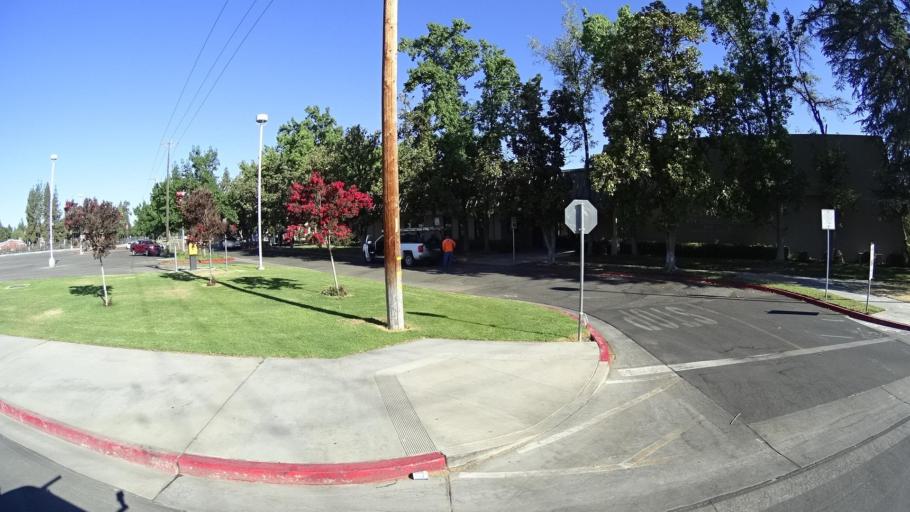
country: US
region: California
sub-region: Fresno County
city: Fresno
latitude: 36.7685
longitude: -119.7923
